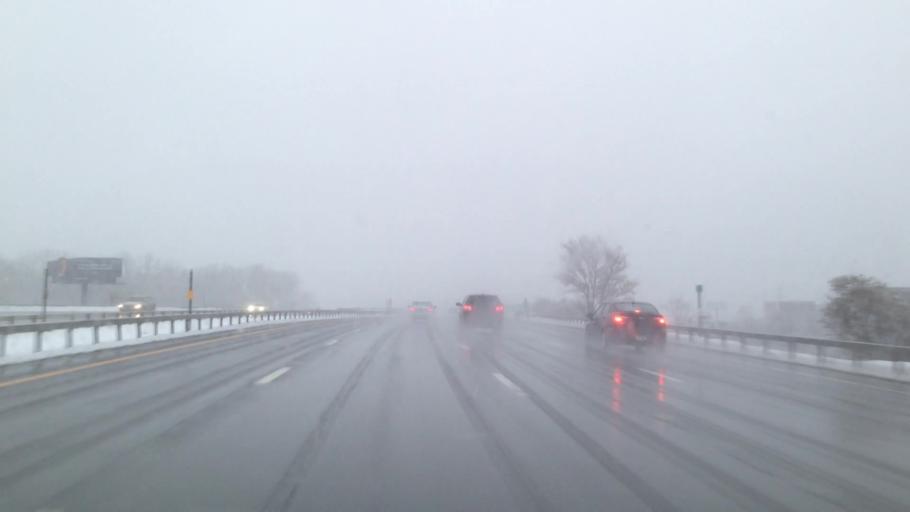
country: US
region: New York
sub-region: Onondaga County
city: East Syracuse
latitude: 43.0594
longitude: -76.0916
